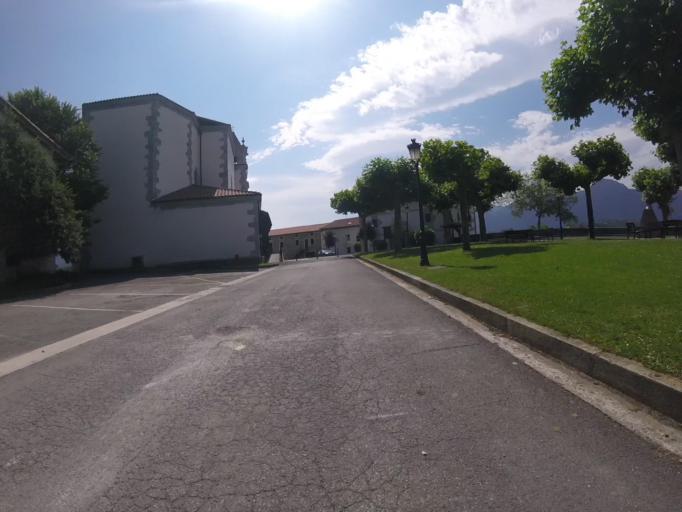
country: ES
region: Basque Country
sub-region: Provincia de Guipuzcoa
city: Orendain
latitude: 43.0796
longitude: -2.1140
